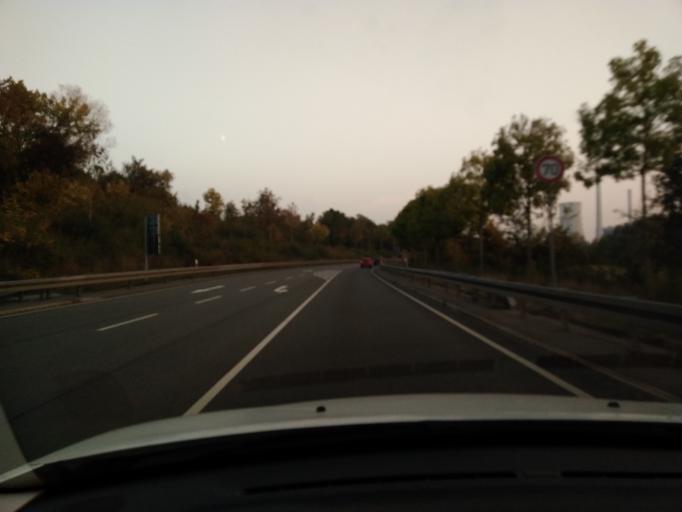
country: DE
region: Saarland
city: Ensdorf
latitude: 49.3048
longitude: 6.7718
